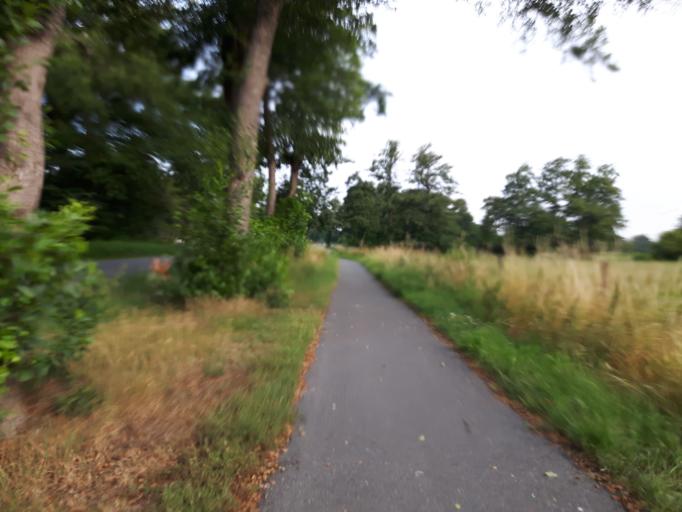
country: DE
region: Lower Saxony
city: Delmenhorst
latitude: 53.0959
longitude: 8.5975
